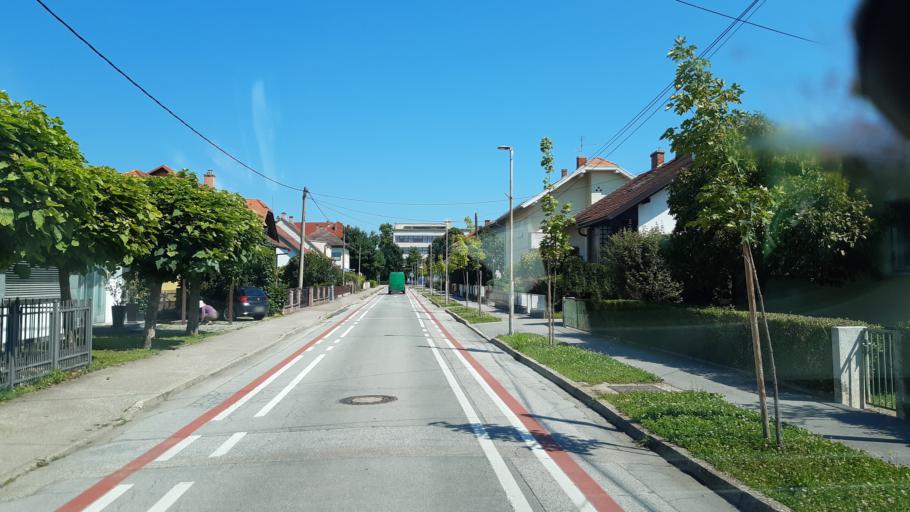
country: SI
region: Murska Sobota
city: Murska Sobota
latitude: 46.6592
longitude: 16.1556
